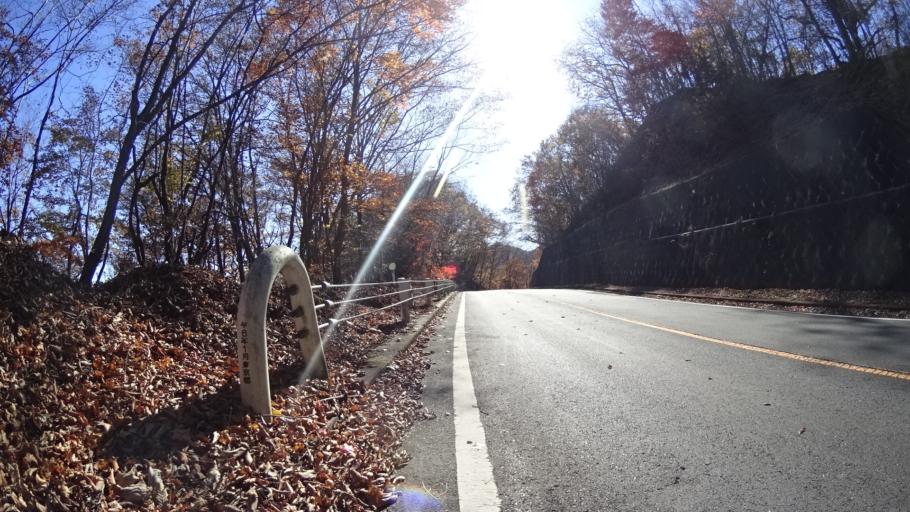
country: JP
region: Yamanashi
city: Uenohara
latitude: 35.7560
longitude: 139.0431
